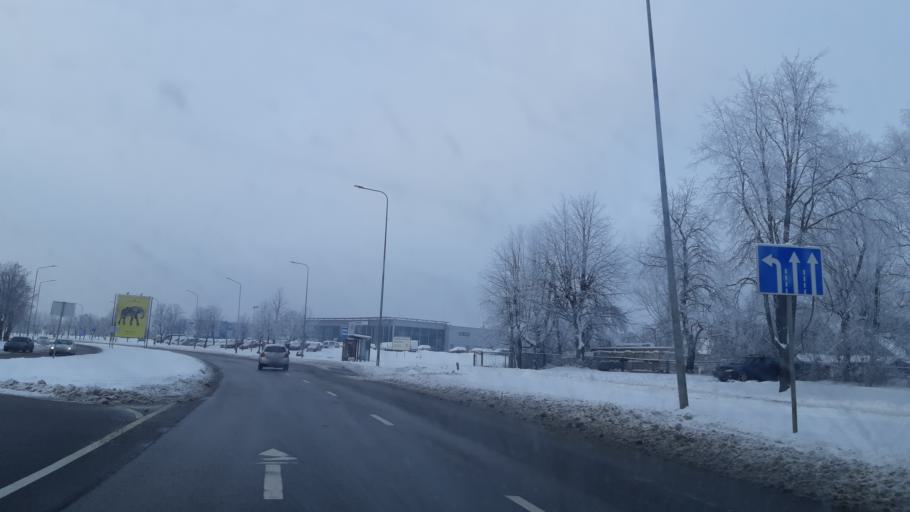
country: LT
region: Kauno apskritis
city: Dainava (Kaunas)
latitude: 54.9298
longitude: 23.9702
